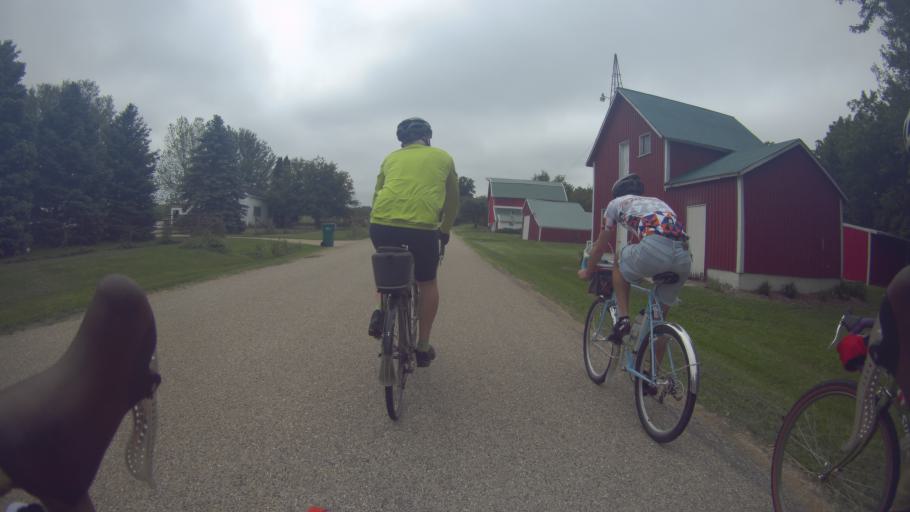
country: US
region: Wisconsin
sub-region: Green County
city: Brooklyn
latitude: 42.8845
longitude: -89.3777
